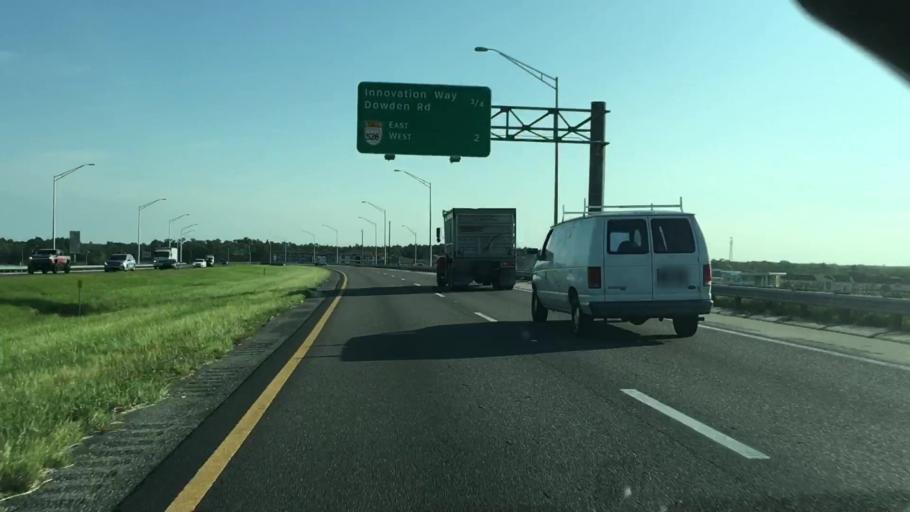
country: US
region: Florida
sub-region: Orange County
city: Conway
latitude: 28.4111
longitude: -81.2292
